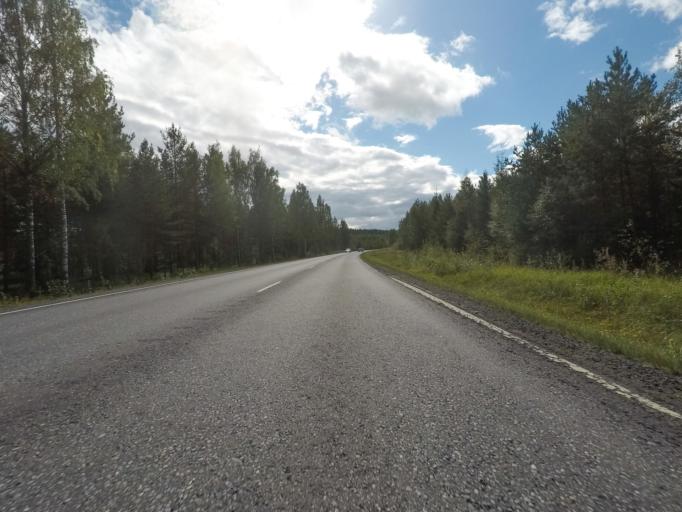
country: FI
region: Central Finland
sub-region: Joutsa
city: Joutsa
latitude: 61.6797
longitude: 26.0526
